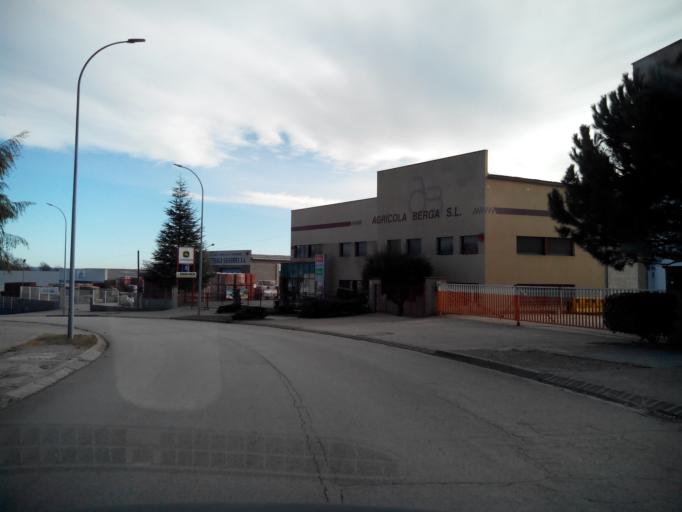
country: ES
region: Catalonia
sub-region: Provincia de Barcelona
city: Berga
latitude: 42.0898
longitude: 1.8261
